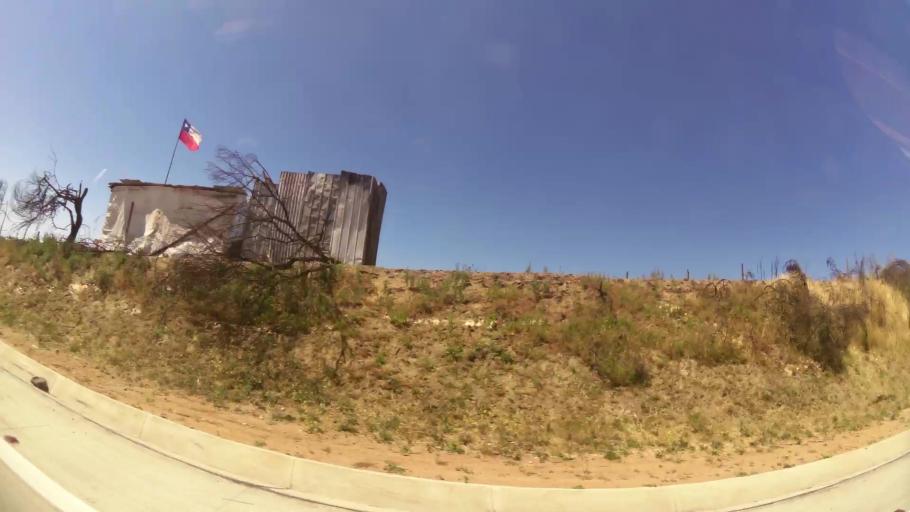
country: CL
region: Valparaiso
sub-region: Provincia de Valparaiso
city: Valparaiso
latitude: -33.0592
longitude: -71.6460
